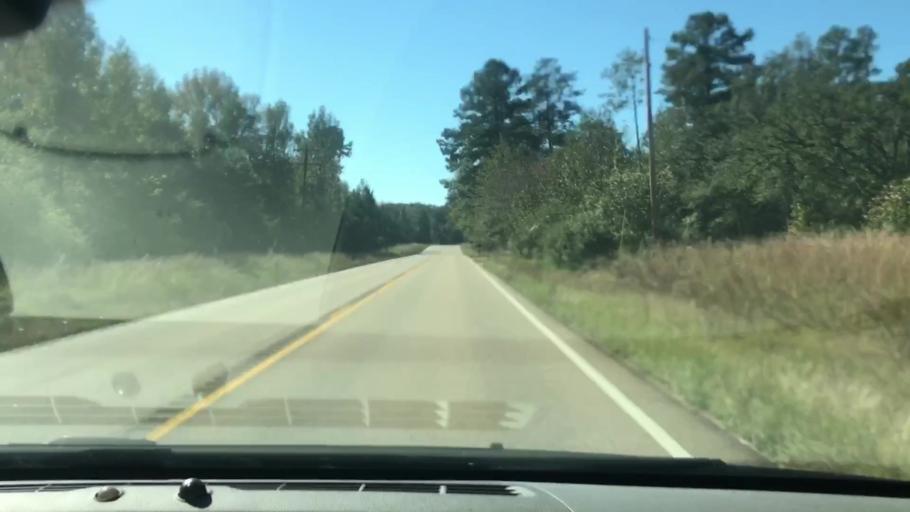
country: US
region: Louisiana
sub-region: Saint Tammany Parish
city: Abita Springs
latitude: 30.5118
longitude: -89.9481
